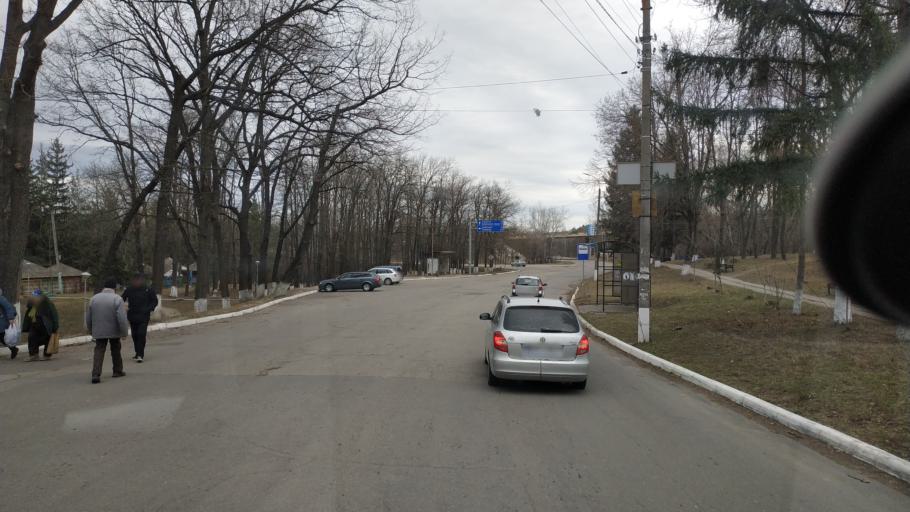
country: MD
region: Chisinau
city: Vadul lui Voda
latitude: 47.0861
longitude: 29.0855
